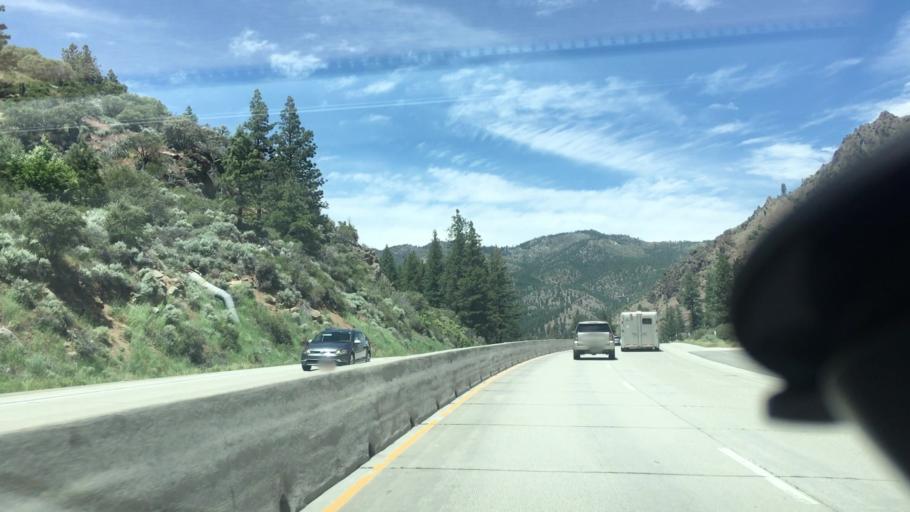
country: US
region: Nevada
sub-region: Washoe County
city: Verdi
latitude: 39.4125
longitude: -120.0284
